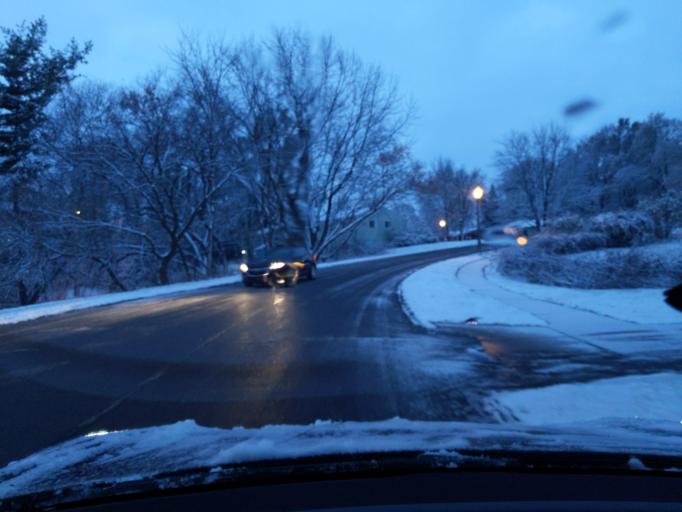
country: US
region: Michigan
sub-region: Ingham County
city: Lansing
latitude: 42.6899
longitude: -84.5620
